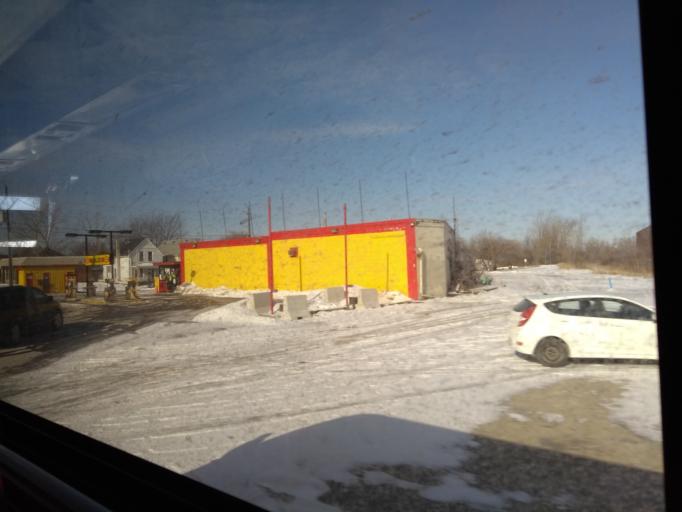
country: CA
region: Ontario
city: Niagara Falls
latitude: 43.1087
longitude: -79.0739
